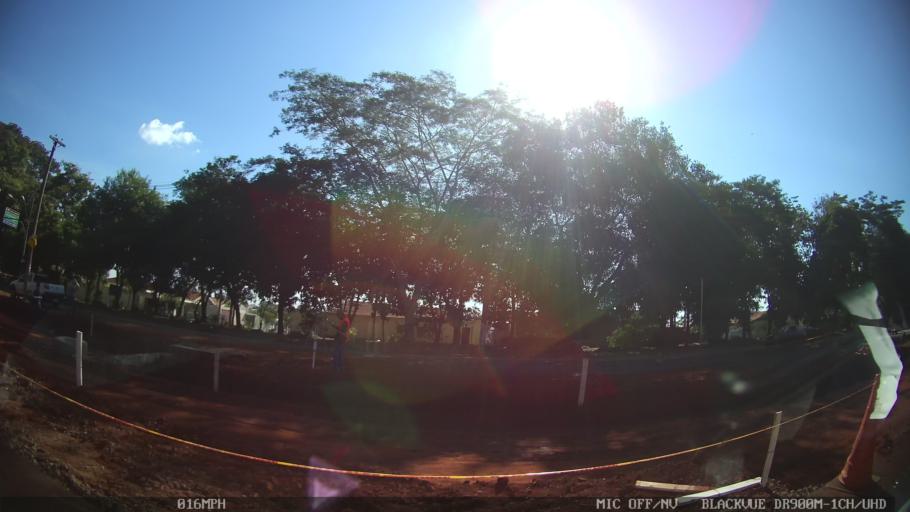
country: BR
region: Sao Paulo
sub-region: Ribeirao Preto
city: Ribeirao Preto
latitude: -21.1627
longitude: -47.7890
